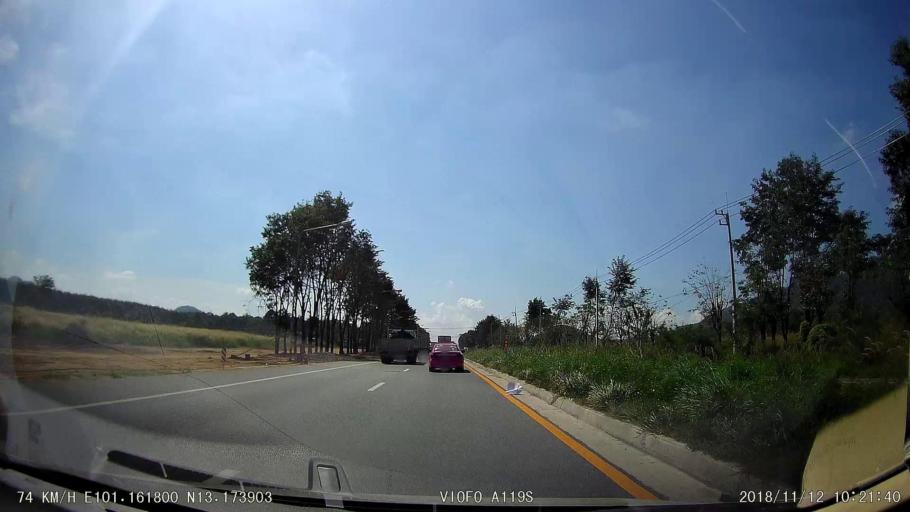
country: TH
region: Chon Buri
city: Ban Bueng
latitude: 13.1737
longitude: 101.1618
